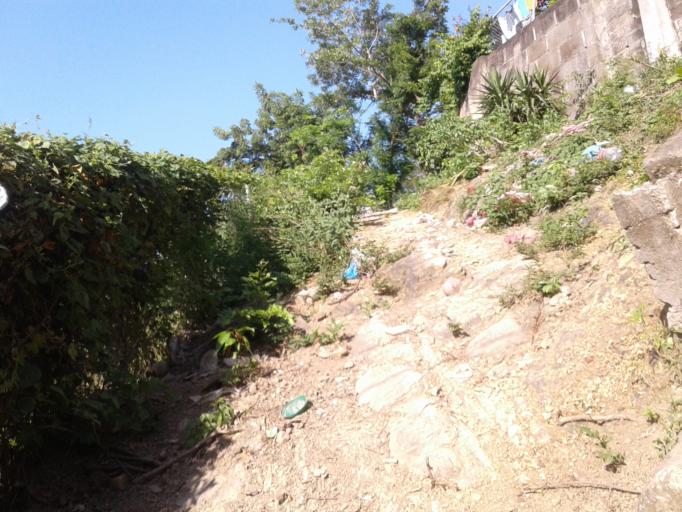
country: NI
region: Rivas
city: San Juan del Sur
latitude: 11.2494
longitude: -85.8722
